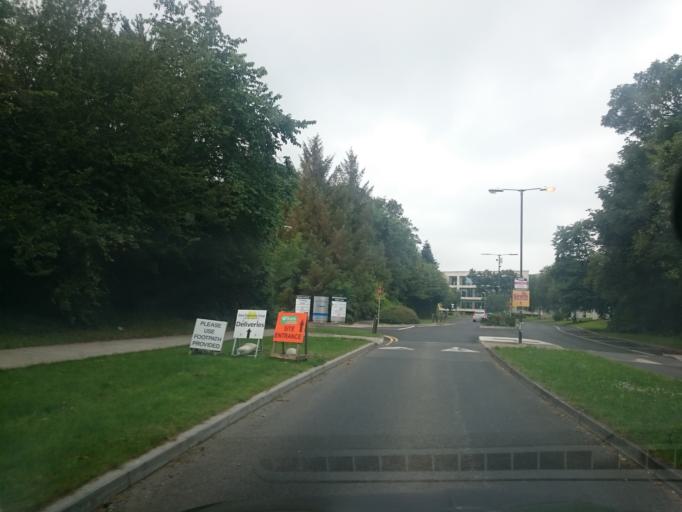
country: IE
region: Leinster
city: Sandyford
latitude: 53.2713
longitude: -6.1998
